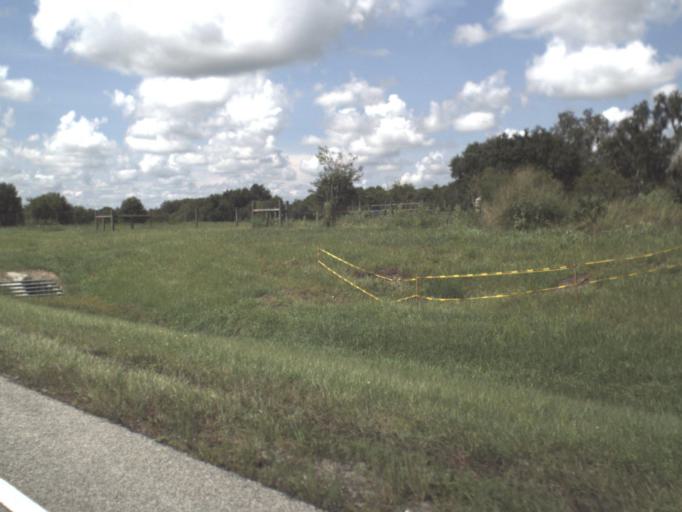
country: US
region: Florida
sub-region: DeSoto County
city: Arcadia
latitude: 27.2848
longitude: -81.8298
